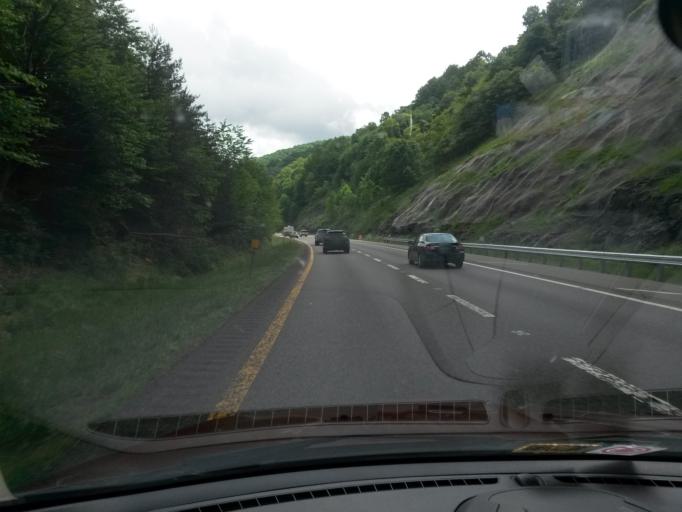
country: US
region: Virginia
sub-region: Carroll County
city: Cana
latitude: 36.6147
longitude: -80.7407
